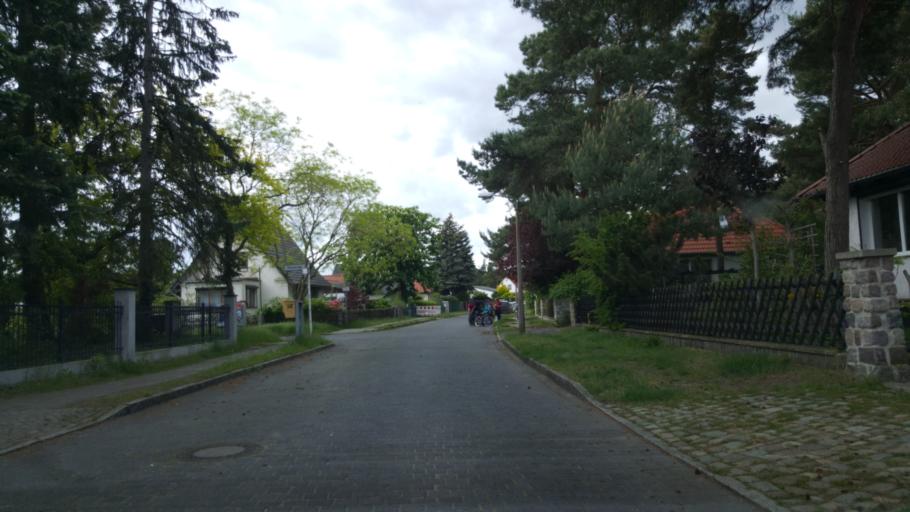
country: DE
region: Berlin
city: Berlin Koepenick
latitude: 52.4448
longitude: 13.5997
